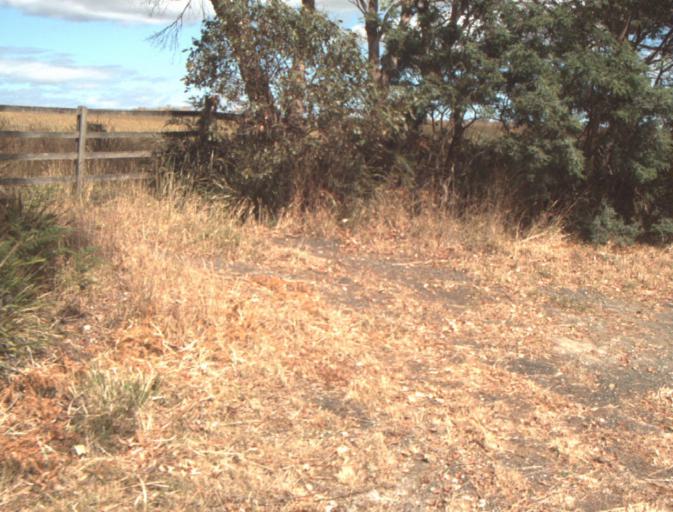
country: AU
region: Tasmania
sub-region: Launceston
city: Mayfield
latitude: -41.2046
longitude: 147.0951
